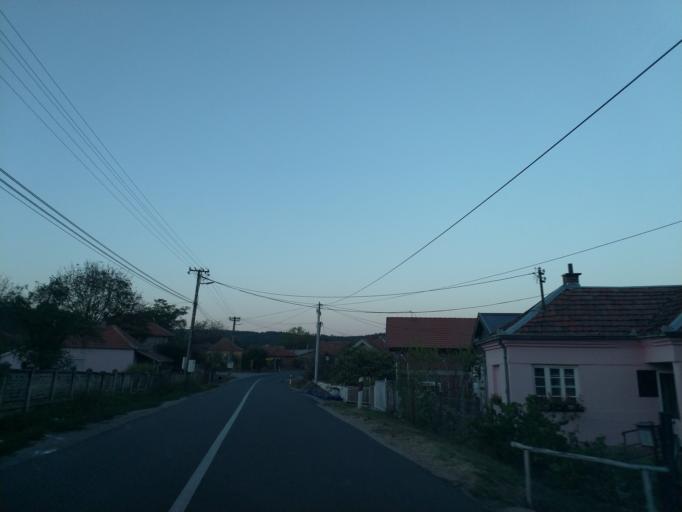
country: RS
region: Central Serbia
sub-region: Rasinski Okrug
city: Krusevac
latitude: 43.6178
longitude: 21.3035
